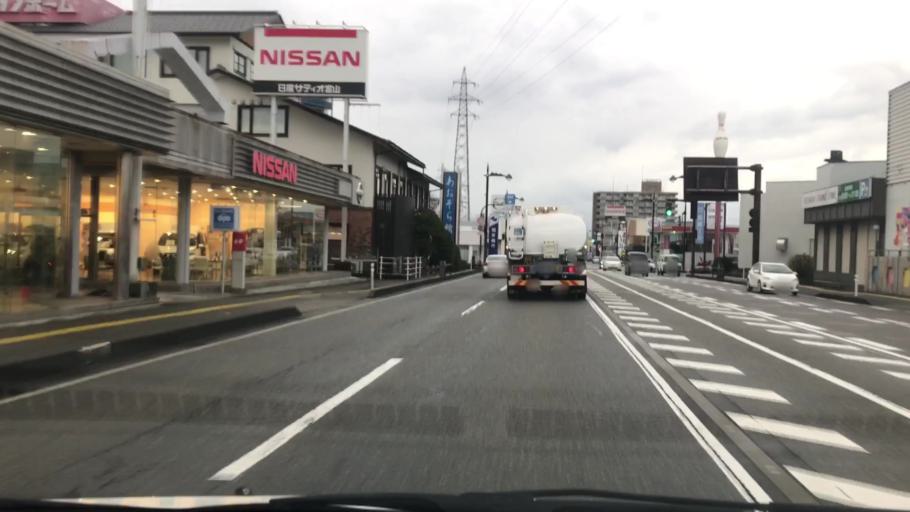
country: JP
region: Toyama
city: Toyama-shi
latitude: 36.6691
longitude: 137.2103
